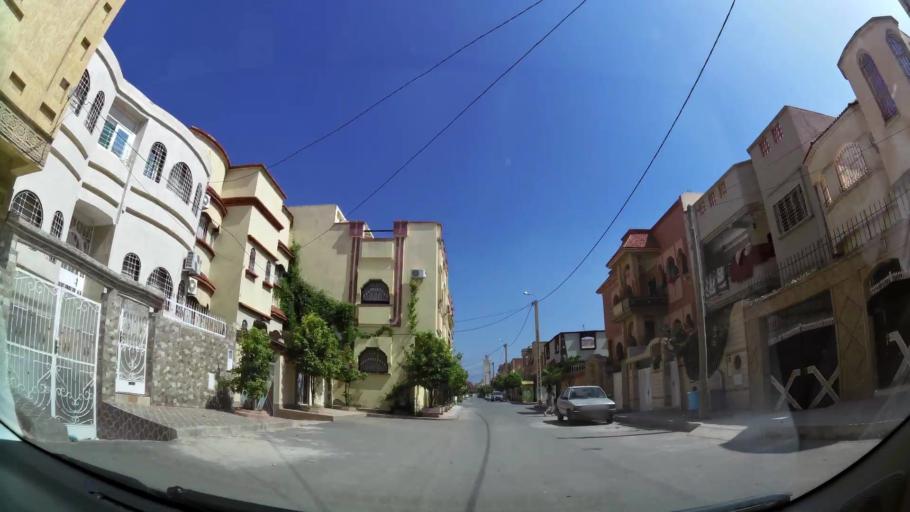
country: MA
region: Oriental
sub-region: Oujda-Angad
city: Oujda
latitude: 34.6890
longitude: -1.8761
